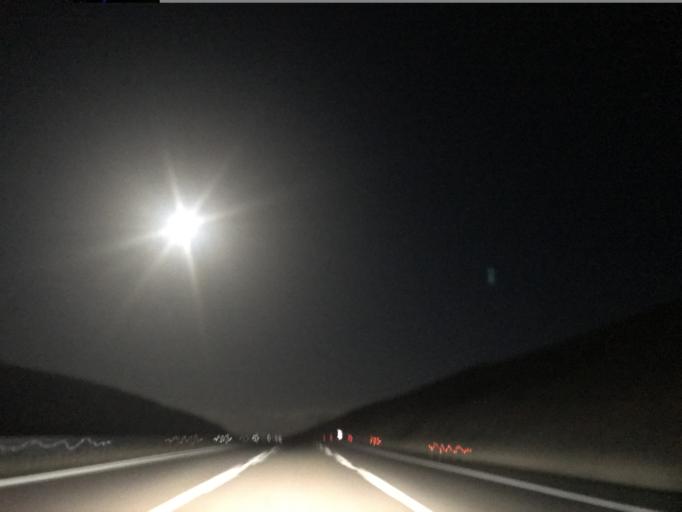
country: TR
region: Nigde
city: Ulukisla
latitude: 37.6359
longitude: 34.4087
